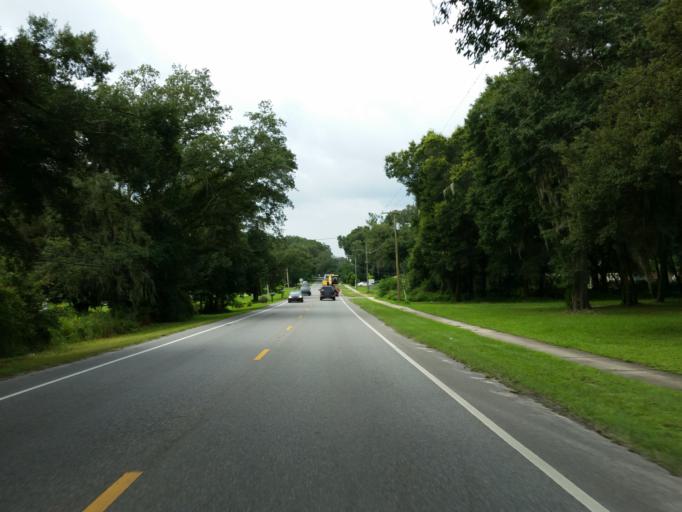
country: US
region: Florida
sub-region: Hillsborough County
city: Thonotosassa
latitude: 28.0287
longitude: -82.3026
